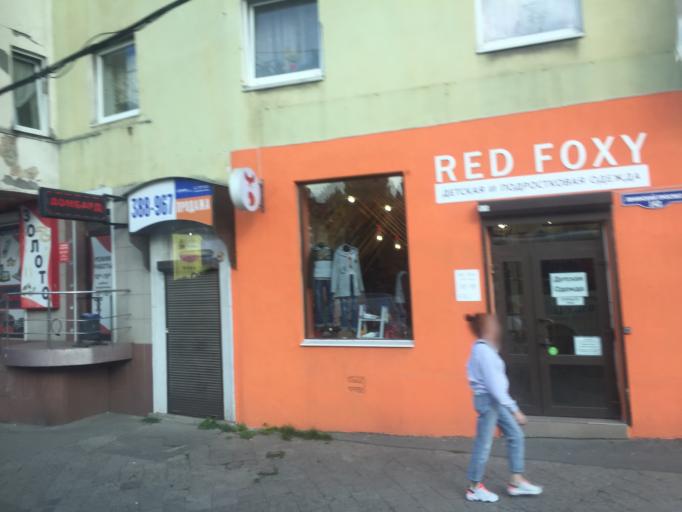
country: RU
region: Kaliningrad
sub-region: Gorod Kaliningrad
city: Kaliningrad
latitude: 54.6977
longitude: 20.5030
